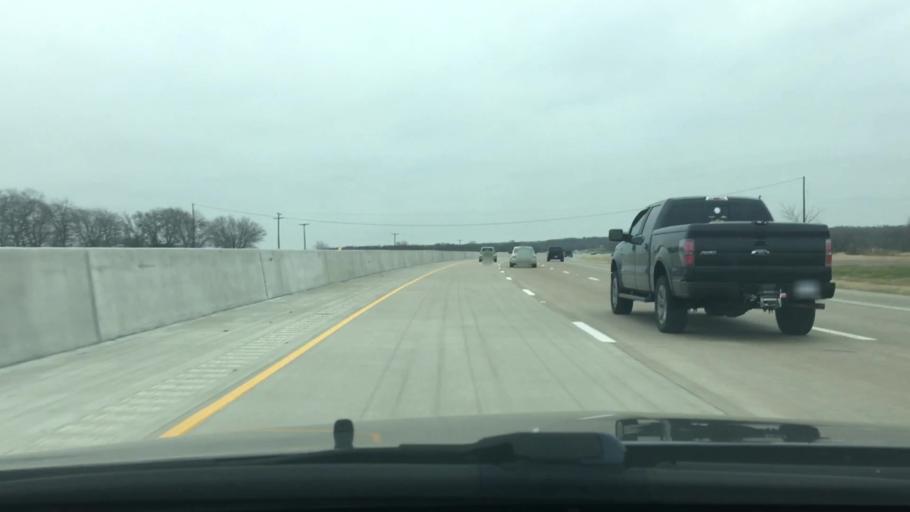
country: US
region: Texas
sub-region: Freestone County
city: Wortham
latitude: 31.9269
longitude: -96.4170
